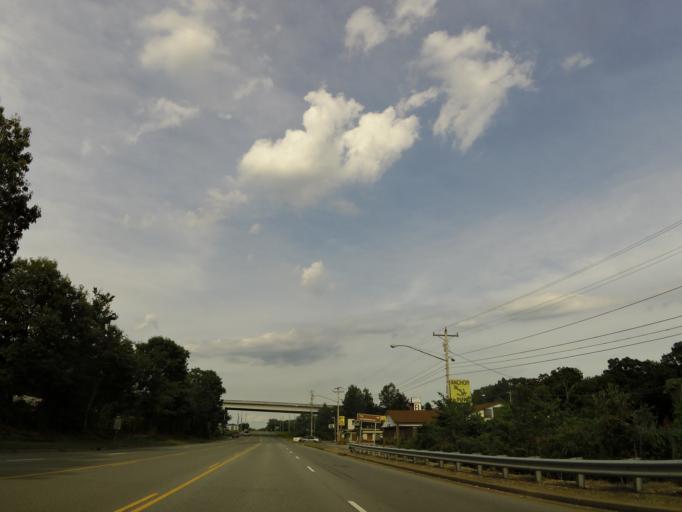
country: US
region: Tennessee
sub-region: Humphreys County
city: New Johnsonville
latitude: 36.0186
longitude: -87.9857
